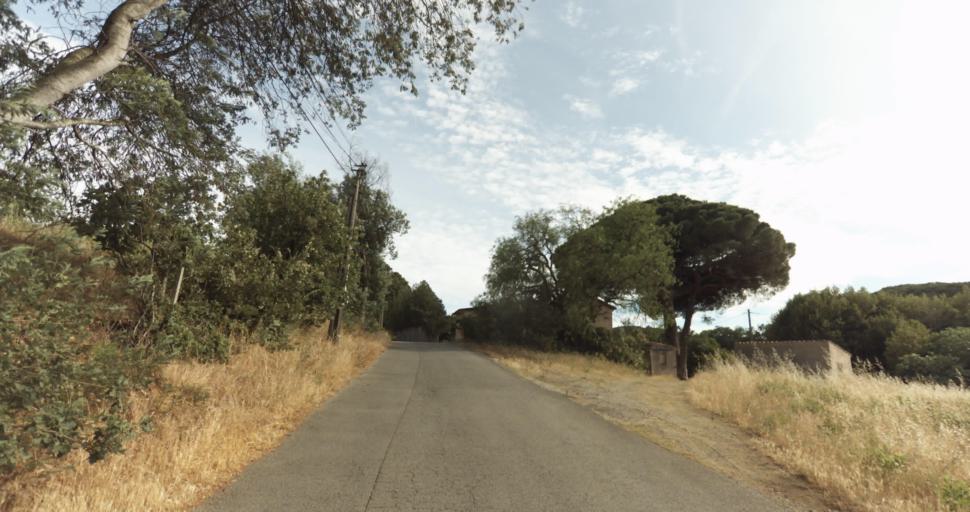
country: FR
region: Provence-Alpes-Cote d'Azur
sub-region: Departement du Var
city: Gassin
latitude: 43.2218
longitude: 6.5805
